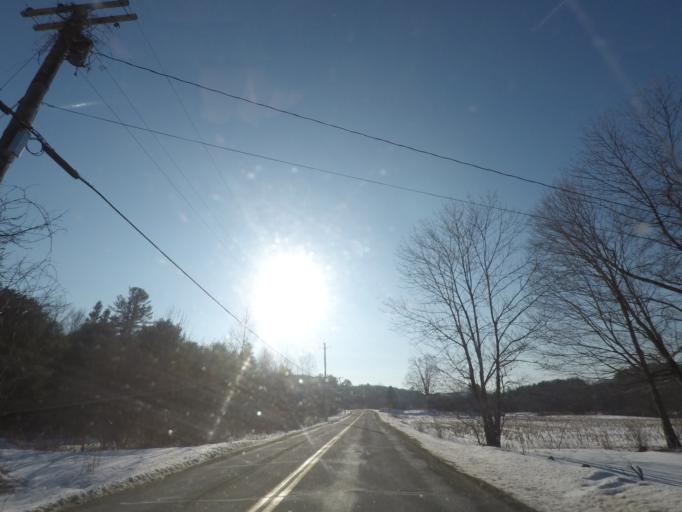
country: US
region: Massachusetts
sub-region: Berkshire County
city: Richmond
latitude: 42.5101
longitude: -73.4249
